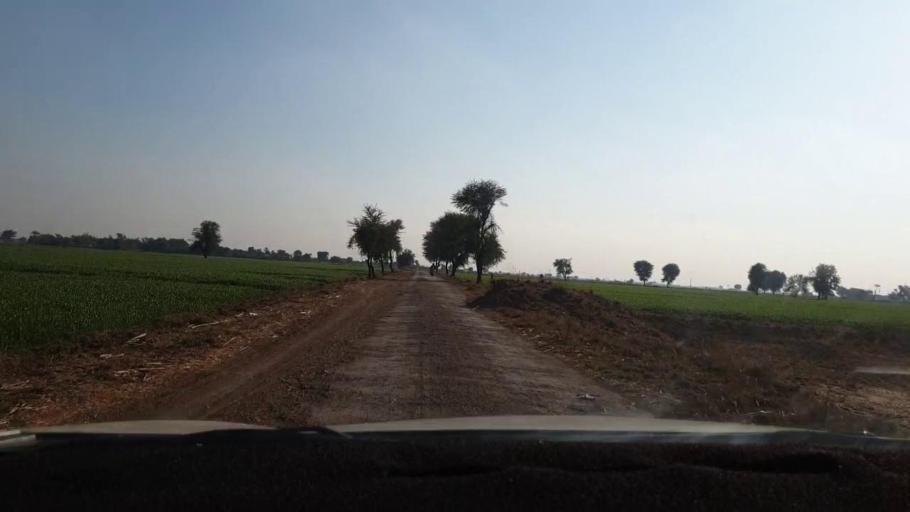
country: PK
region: Sindh
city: Berani
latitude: 25.7681
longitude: 68.7685
